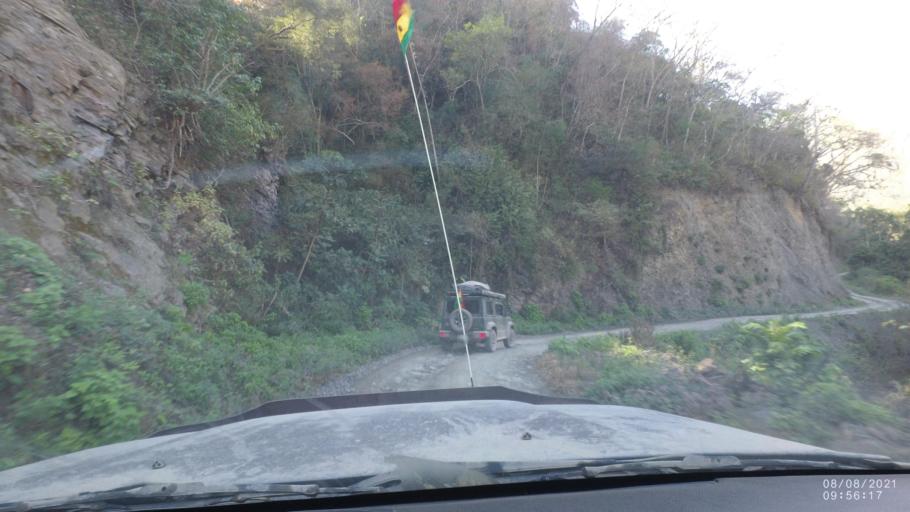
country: BO
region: La Paz
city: Quime
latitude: -16.6374
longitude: -66.7265
